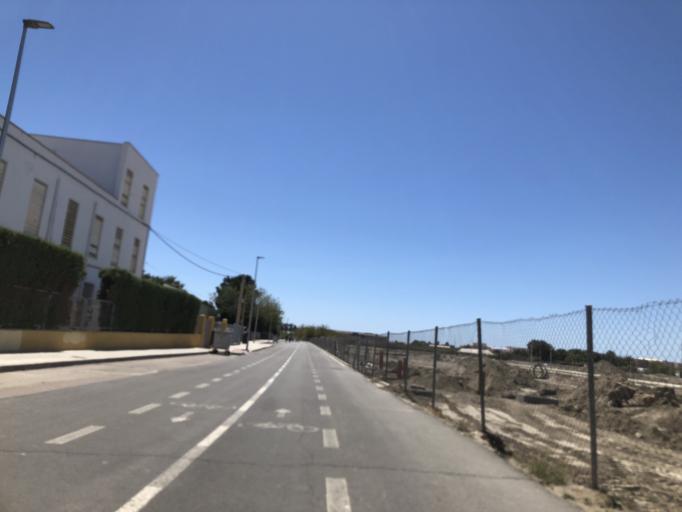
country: ES
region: Andalusia
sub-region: Provincia de Almeria
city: Almeria
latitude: 36.8376
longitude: -2.4053
